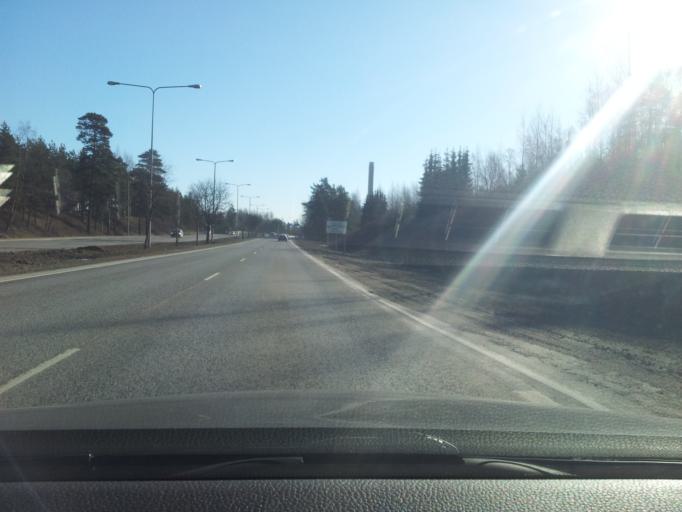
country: FI
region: Uusimaa
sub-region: Helsinki
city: Vantaa
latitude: 60.2280
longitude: 25.0688
